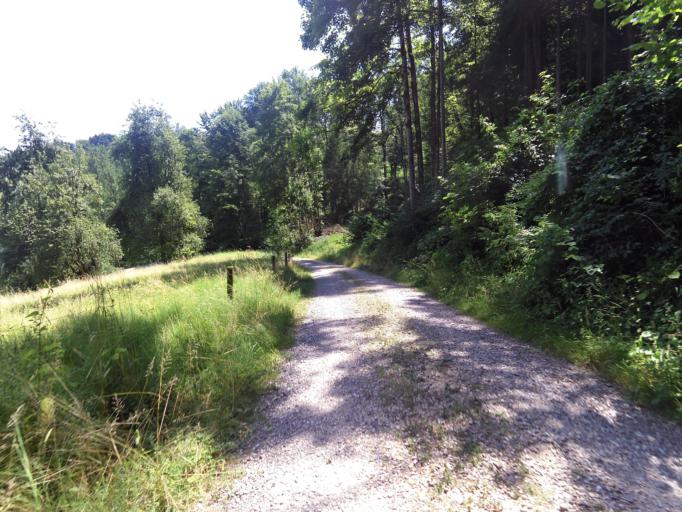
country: CH
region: Thurgau
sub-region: Frauenfeld District
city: Mullheim
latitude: 47.5780
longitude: 9.0064
